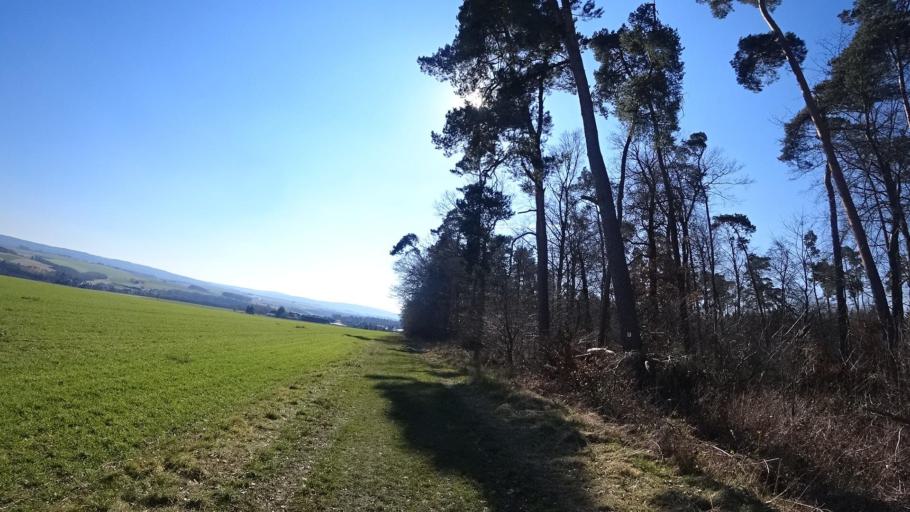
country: DE
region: Rheinland-Pfalz
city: Schonborn
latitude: 49.9517
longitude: 7.4709
